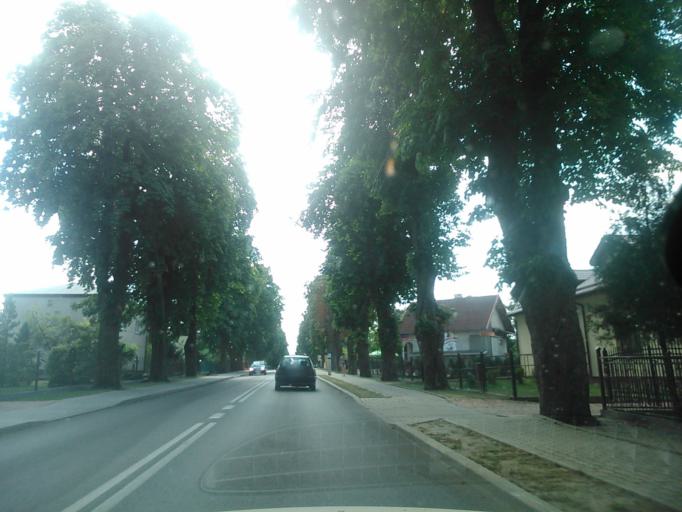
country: PL
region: Warmian-Masurian Voivodeship
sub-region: Powiat dzialdowski
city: Ilowo -Osada
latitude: 53.1738
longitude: 20.2975
